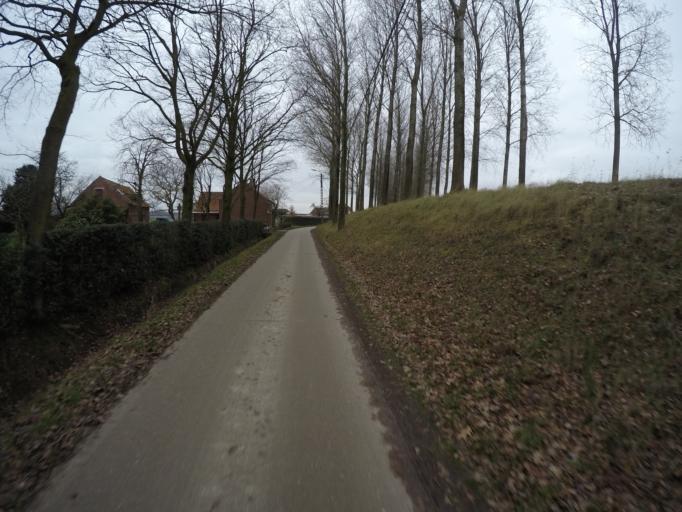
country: BE
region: Flanders
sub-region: Provincie Oost-Vlaanderen
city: Sint-Gillis-Waas
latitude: 51.2468
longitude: 4.1218
